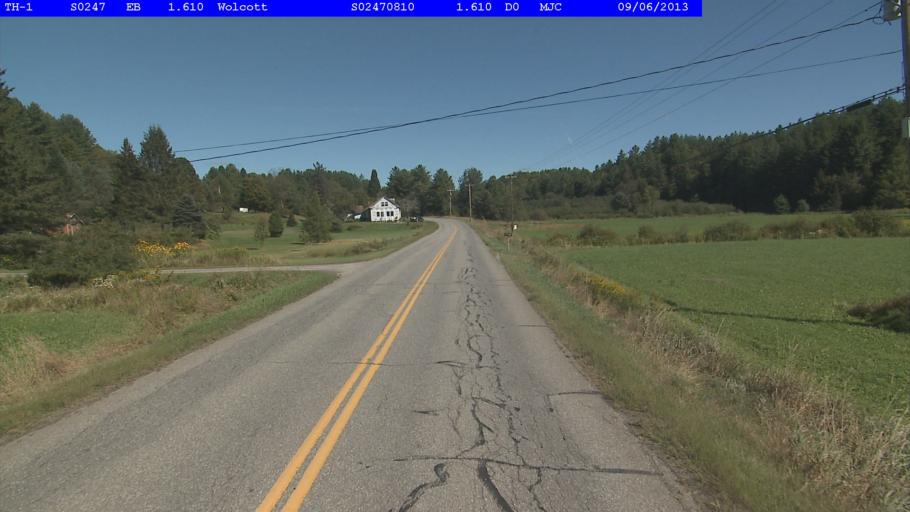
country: US
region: Vermont
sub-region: Lamoille County
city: Morrisville
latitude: 44.5790
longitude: -72.4762
